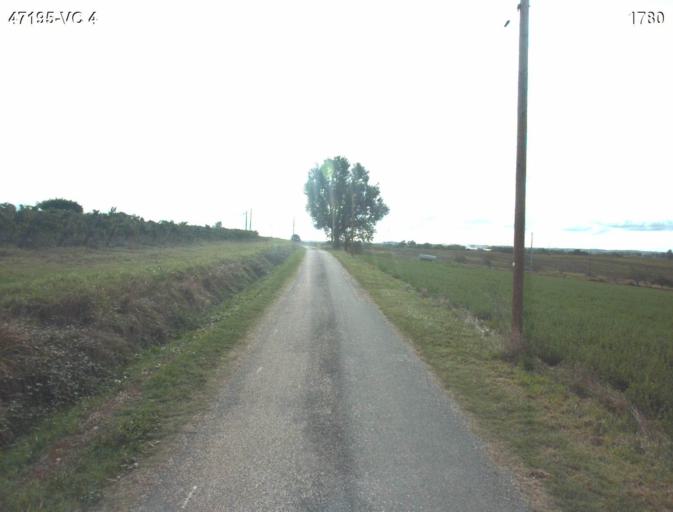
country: FR
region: Aquitaine
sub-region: Departement du Lot-et-Garonne
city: Nerac
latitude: 44.1073
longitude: 0.3864
